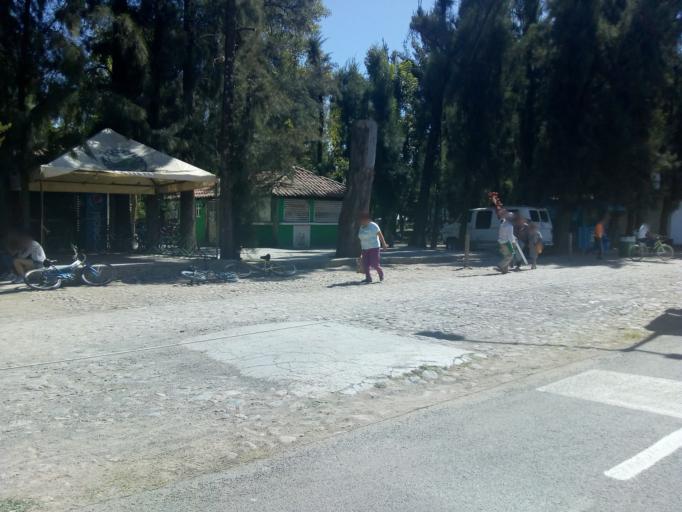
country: MX
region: Guanajuato
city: Leon
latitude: 21.1730
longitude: -101.6870
